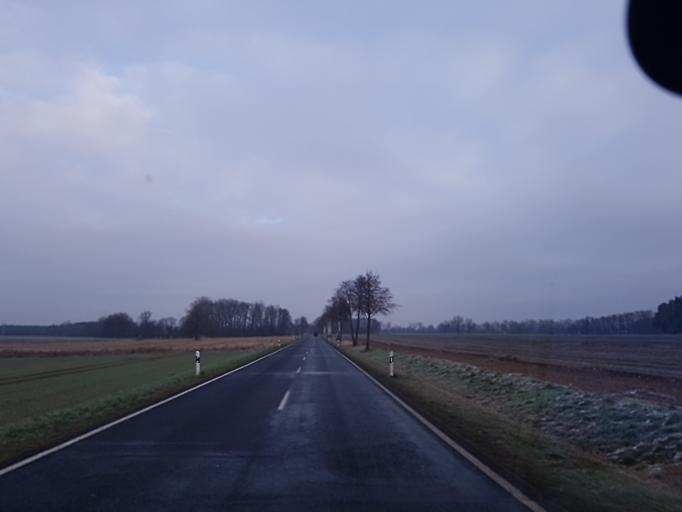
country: DE
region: Brandenburg
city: Crinitz
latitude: 51.7494
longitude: 13.8562
